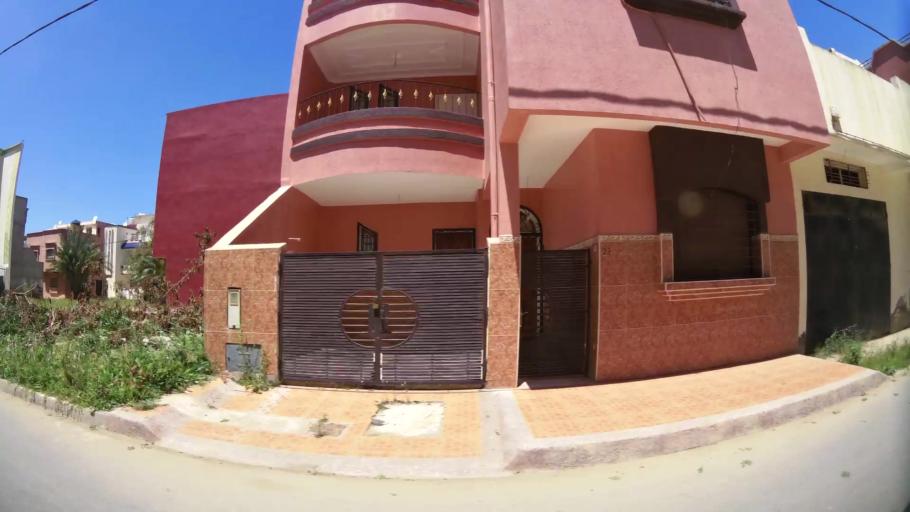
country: MA
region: Oriental
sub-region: Berkane-Taourirt
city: Madagh
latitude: 35.0776
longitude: -2.2285
